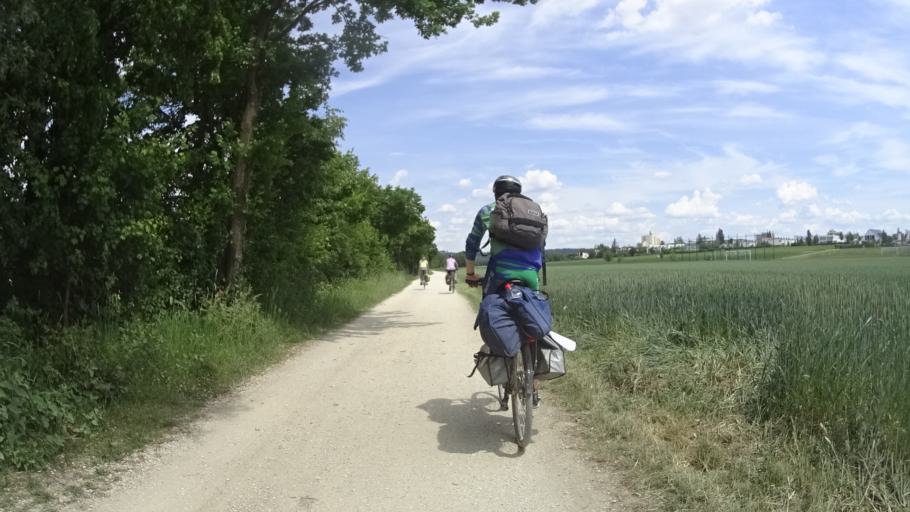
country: DE
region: Bavaria
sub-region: Upper Palatinate
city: Sinzing
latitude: 49.0144
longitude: 12.0317
